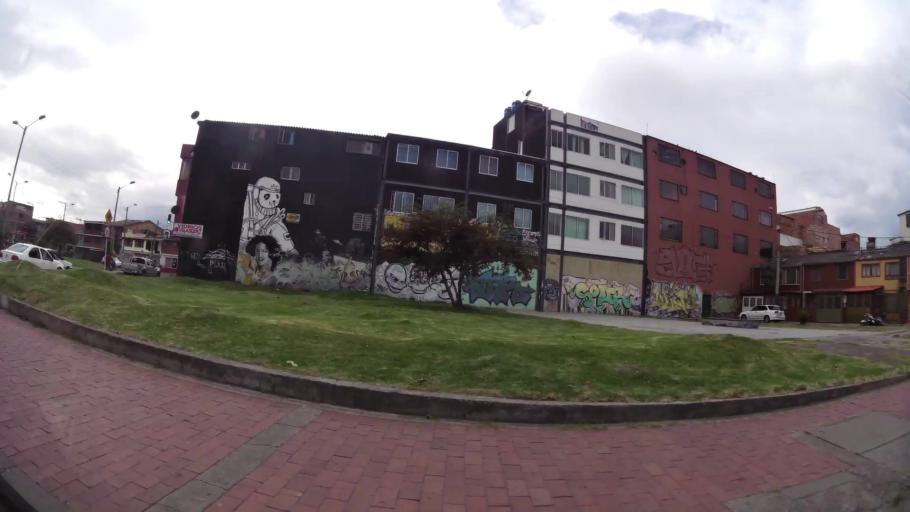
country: CO
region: Bogota D.C.
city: Bogota
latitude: 4.6073
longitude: -74.1371
